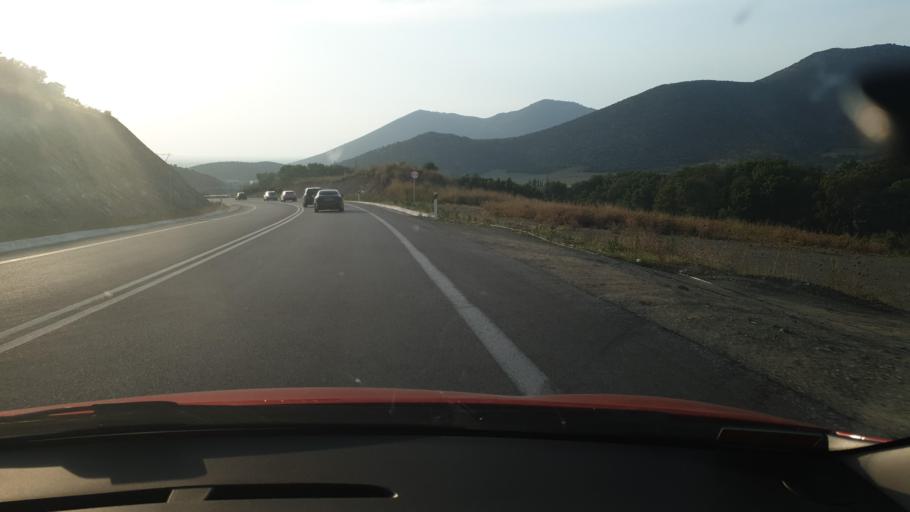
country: GR
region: Central Macedonia
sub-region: Nomos Chalkidikis
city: Galatista
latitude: 40.4635
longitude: 23.2202
